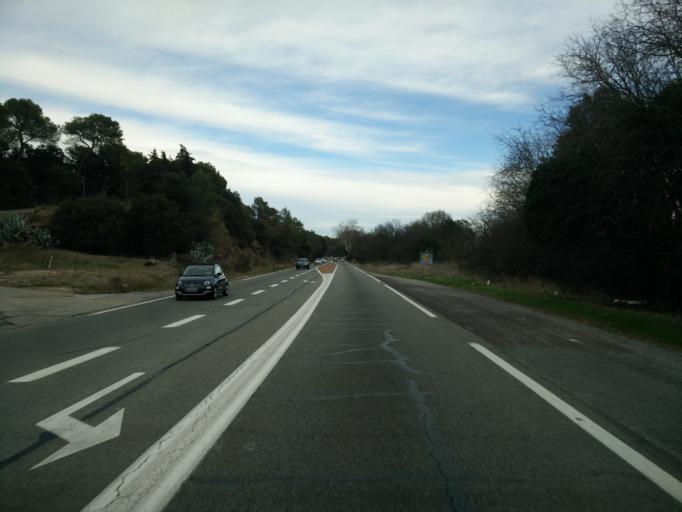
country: FR
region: Provence-Alpes-Cote d'Azur
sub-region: Departement du Var
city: Le Muy
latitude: 43.4674
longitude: 6.6033
